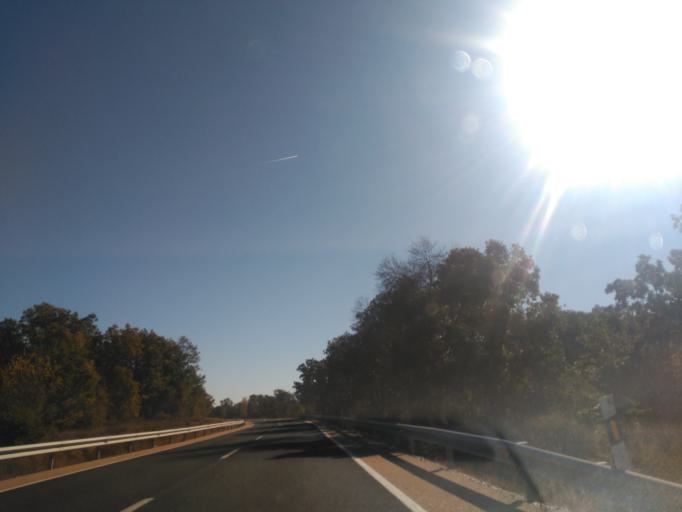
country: ES
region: Castille and Leon
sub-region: Provincia de Soria
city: Cidones
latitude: 41.8100
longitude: -2.6888
